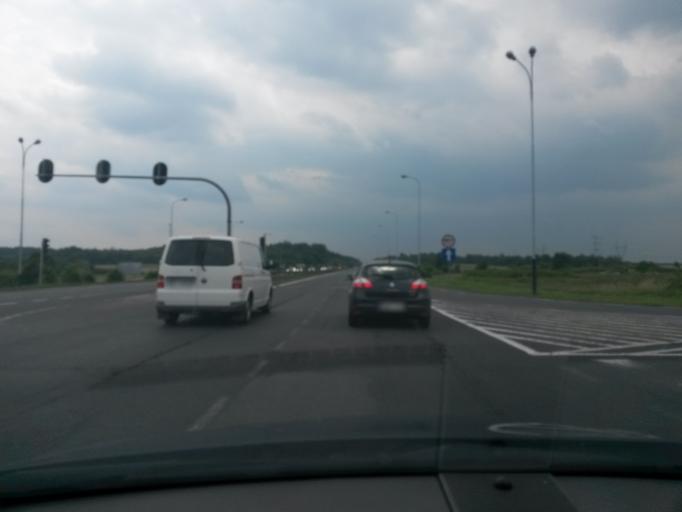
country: PL
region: Lodz Voivodeship
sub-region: Powiat radomszczanski
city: Radomsko
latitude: 51.0800
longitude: 19.3719
